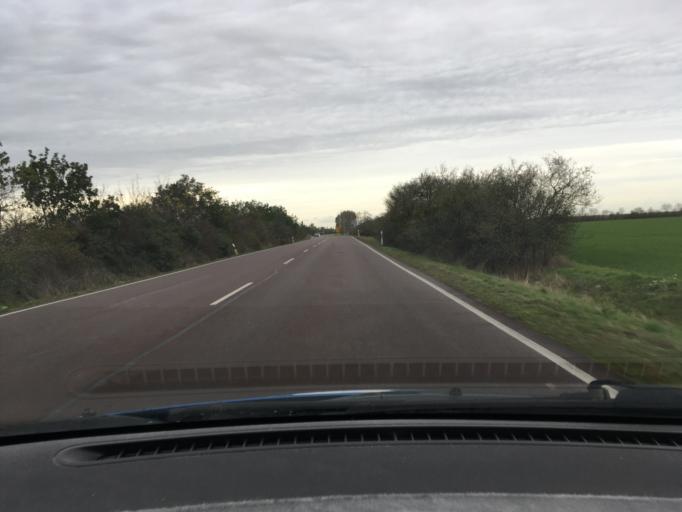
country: DE
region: Saxony-Anhalt
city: Zerbst
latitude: 51.9899
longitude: 12.0457
